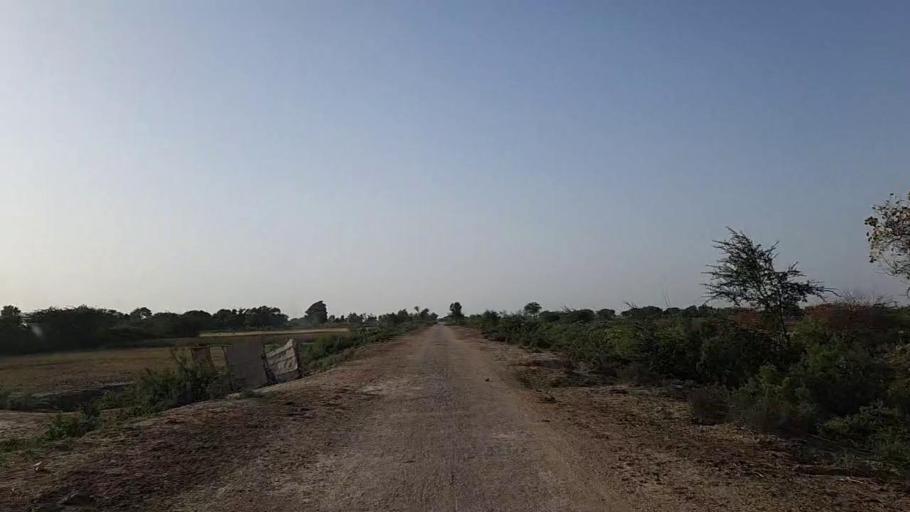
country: PK
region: Sindh
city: Jati
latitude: 24.3241
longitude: 68.1653
